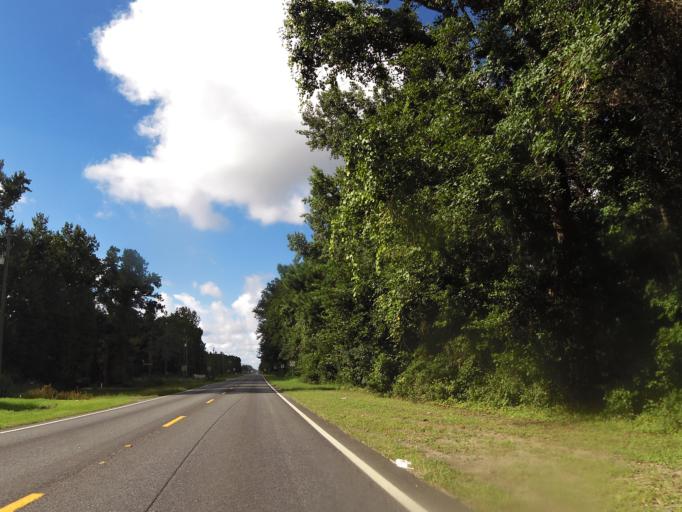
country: US
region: Georgia
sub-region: Camden County
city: Kingsland
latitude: 30.8144
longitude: -81.6930
